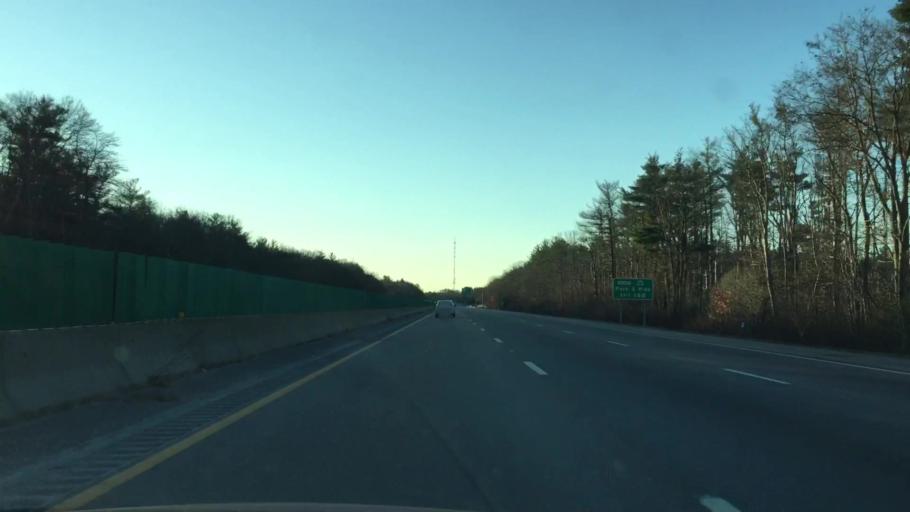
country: US
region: Massachusetts
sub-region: Plymouth County
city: West Bridgewater
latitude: 42.0299
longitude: -71.0509
